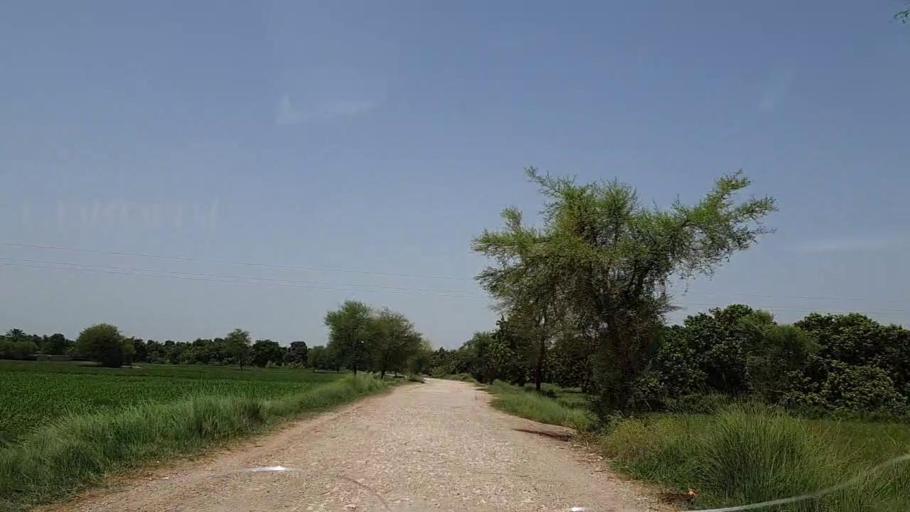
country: PK
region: Sindh
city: Tharu Shah
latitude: 26.9608
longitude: 68.0421
